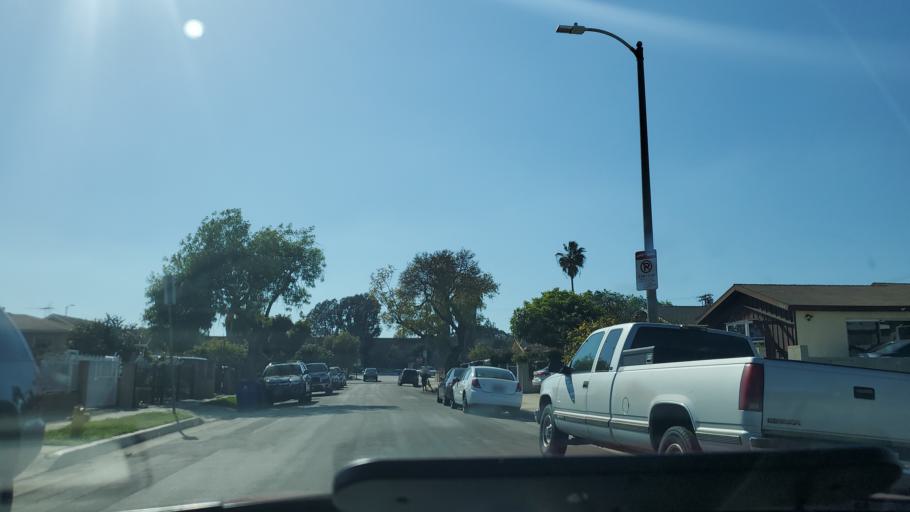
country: US
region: California
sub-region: Los Angeles County
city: West Carson
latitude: 33.7895
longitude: -118.2796
